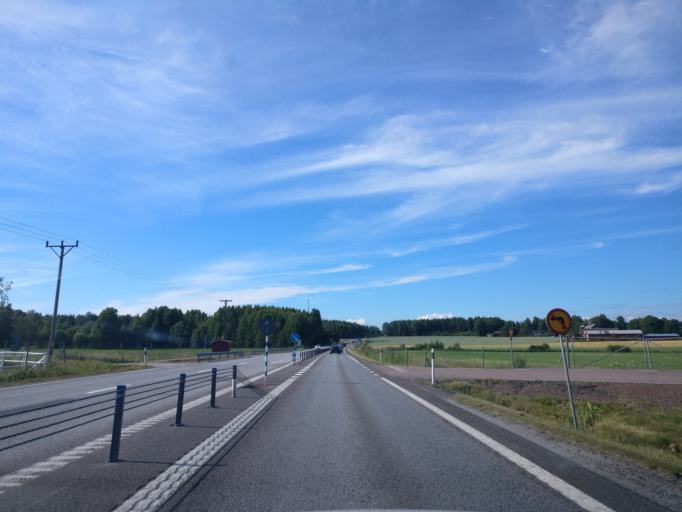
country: SE
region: Vaermland
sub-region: Kils Kommun
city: Kil
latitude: 59.4472
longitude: 13.3789
